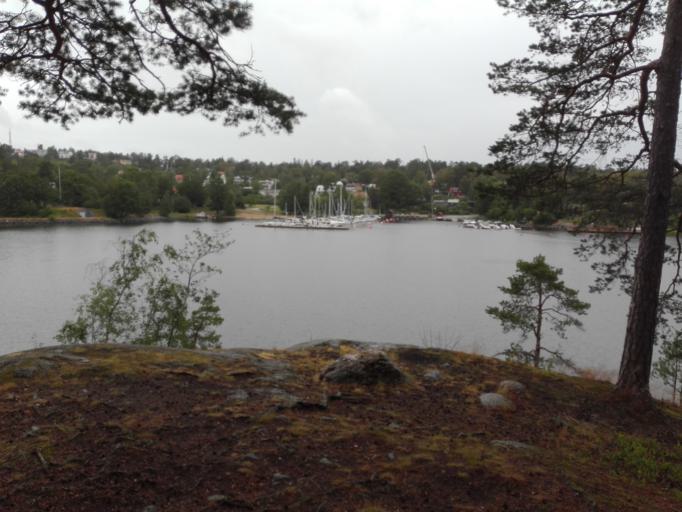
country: SE
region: Stockholm
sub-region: Nacka Kommun
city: Fisksatra
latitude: 59.2972
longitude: 18.2569
